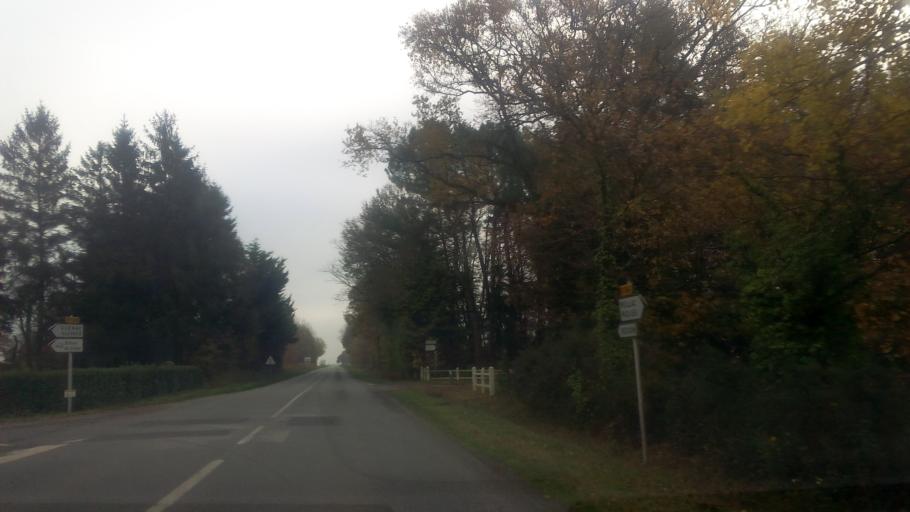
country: FR
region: Brittany
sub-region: Departement du Morbihan
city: Peillac
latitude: 47.7142
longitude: -2.1865
